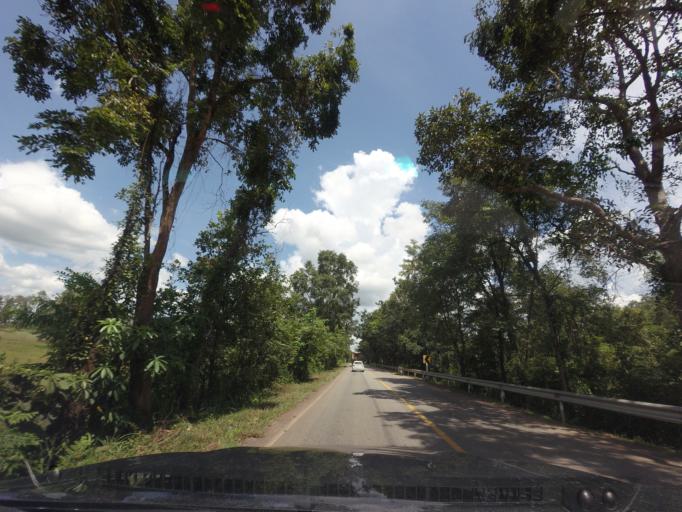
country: TH
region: Changwat Udon Thani
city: Phibun Rak
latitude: 17.5825
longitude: 103.0383
